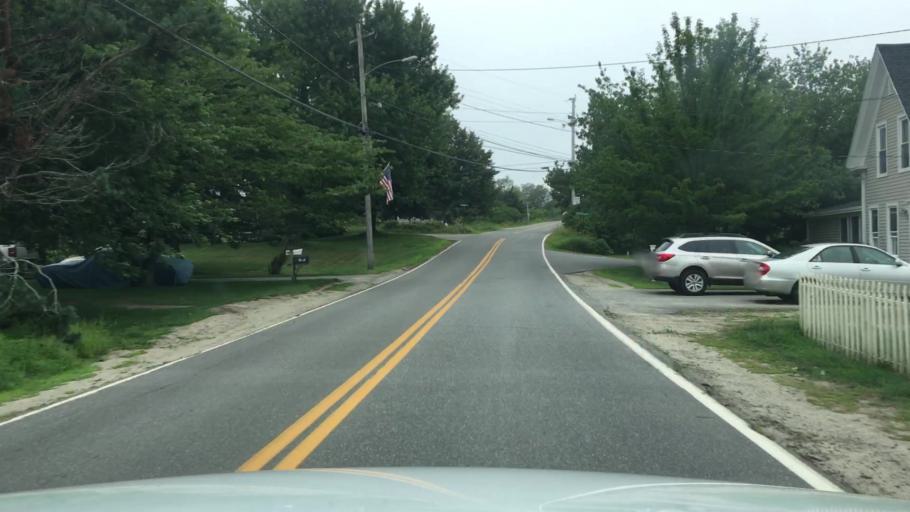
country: US
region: Maine
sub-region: Cumberland County
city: Harpswell Center
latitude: 43.7281
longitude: -69.9961
